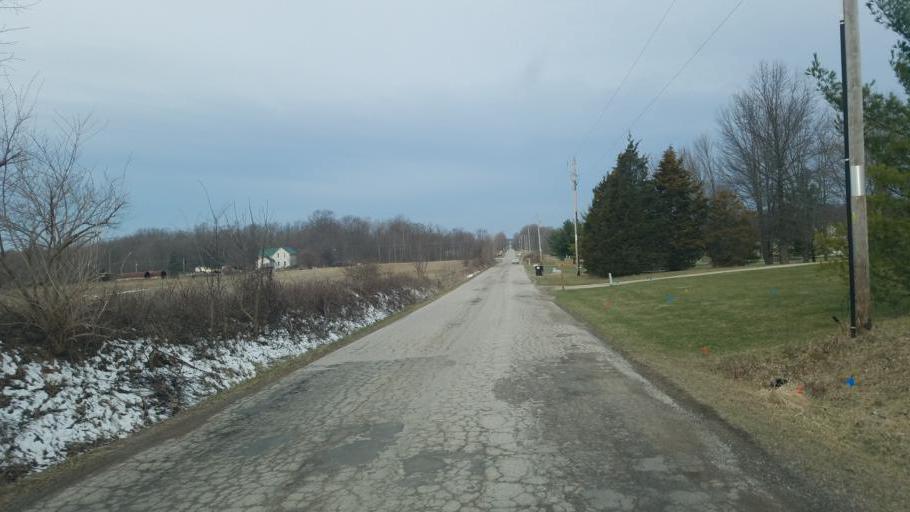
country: US
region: Ohio
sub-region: Morrow County
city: Mount Gilead
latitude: 40.4950
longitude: -82.8159
